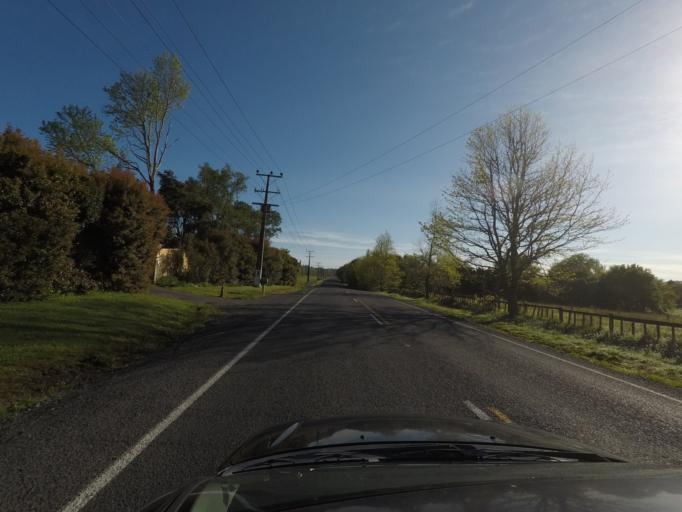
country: NZ
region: Auckland
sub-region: Auckland
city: Red Hill
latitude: -37.0115
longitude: 174.9511
